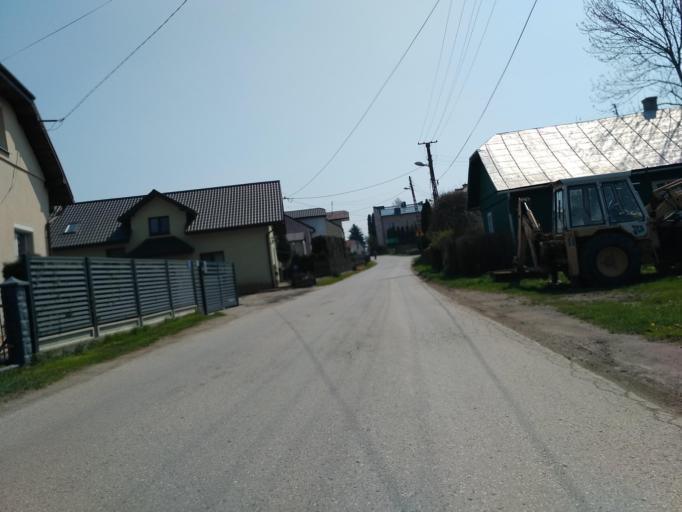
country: PL
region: Subcarpathian Voivodeship
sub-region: Powiat sanocki
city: Zarszyn
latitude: 49.5842
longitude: 22.0132
